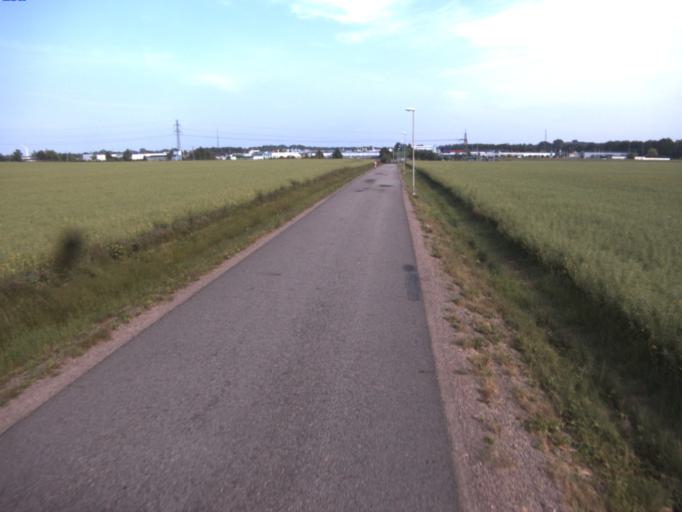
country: SE
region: Skane
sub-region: Helsingborg
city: Odakra
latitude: 56.0787
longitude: 12.7075
